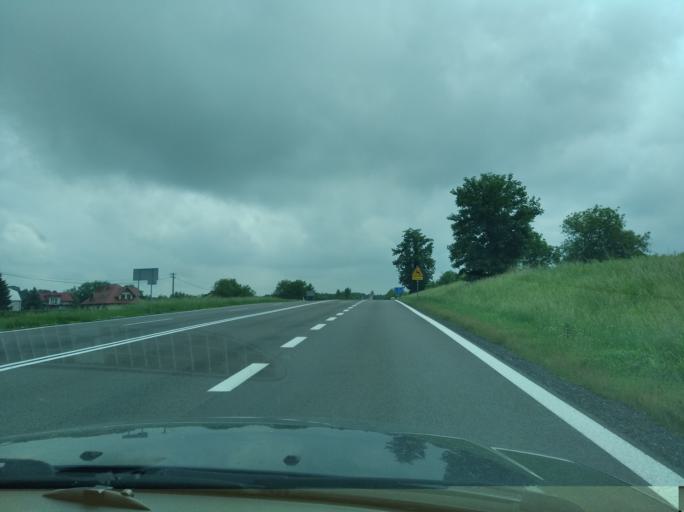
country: PL
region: Subcarpathian Voivodeship
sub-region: Powiat przeworski
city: Rozborz
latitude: 50.0454
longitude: 22.5449
